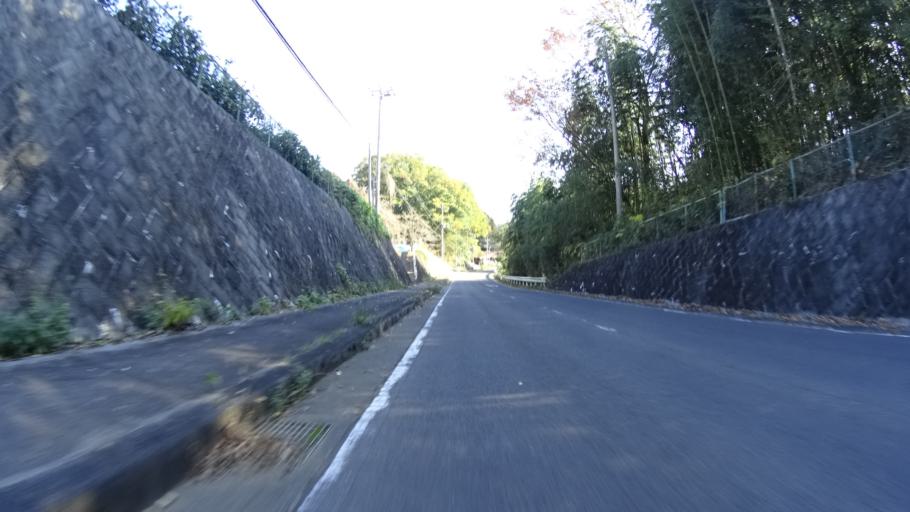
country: JP
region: Yamanashi
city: Uenohara
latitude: 35.6476
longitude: 139.1235
